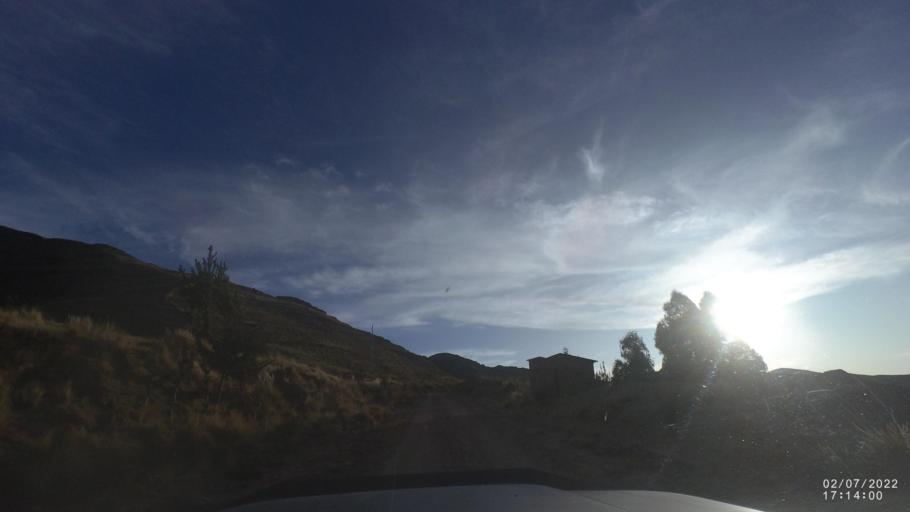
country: BO
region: Cochabamba
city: Irpa Irpa
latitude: -17.8785
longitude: -66.5780
